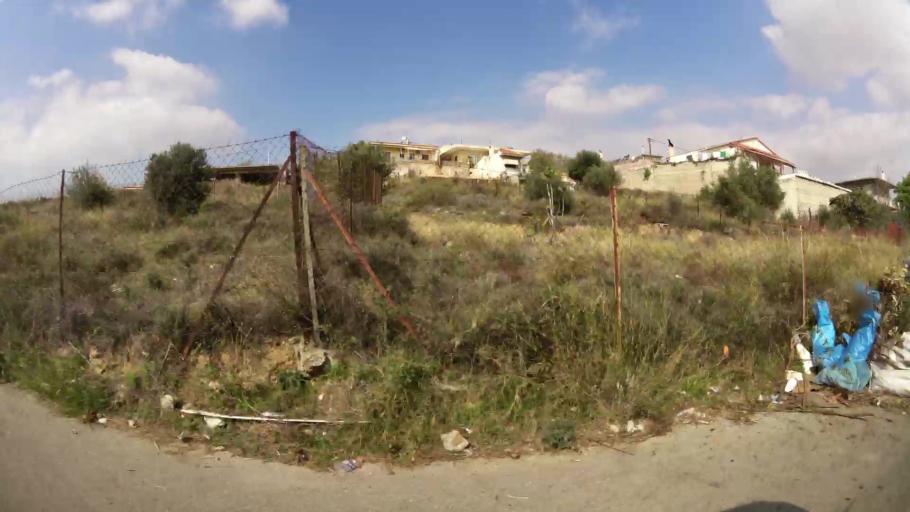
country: GR
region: Attica
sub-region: Nomarchia Dytikis Attikis
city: Zefyri
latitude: 38.0587
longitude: 23.7275
